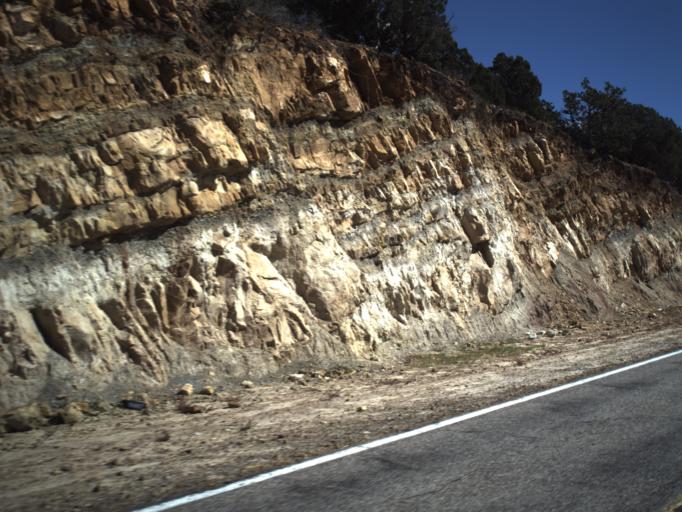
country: US
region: Utah
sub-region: Washington County
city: Enterprise
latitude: 37.5408
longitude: -113.6613
